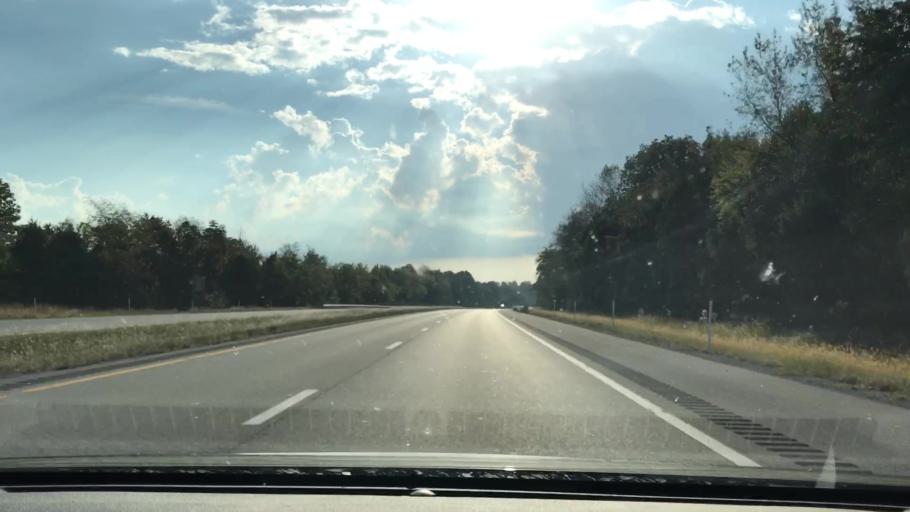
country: US
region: Kentucky
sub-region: Barren County
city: Cave City
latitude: 37.0458
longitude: -86.0764
